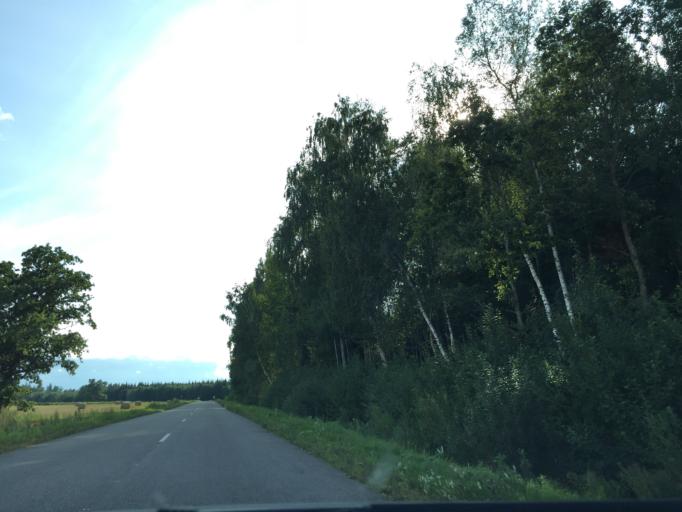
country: LV
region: Kegums
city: Kegums
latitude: 56.8218
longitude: 24.7528
